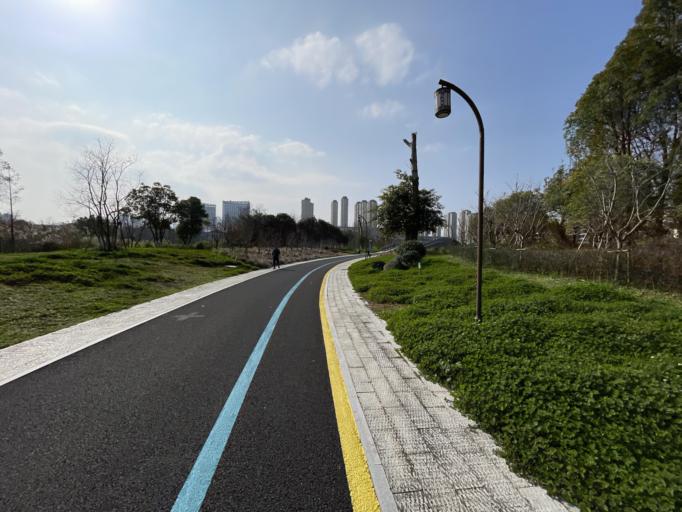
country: CN
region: Zhejiang Sheng
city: Wenzhou
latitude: 27.9561
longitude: 120.6872
